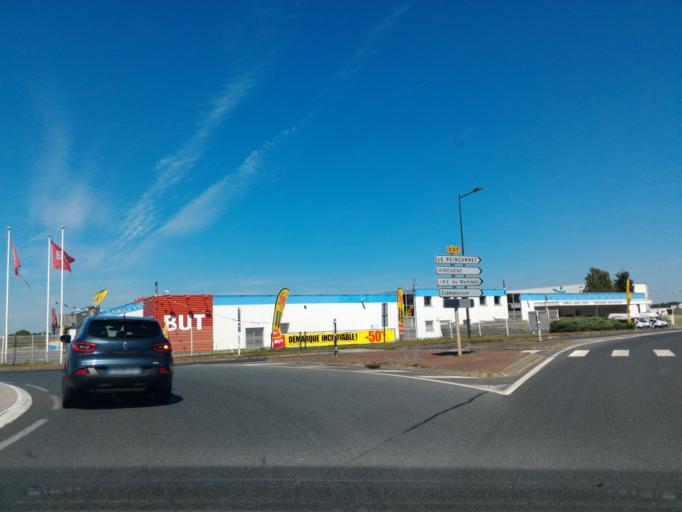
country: FR
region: Centre
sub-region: Departement de l'Indre
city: Saint-Maur
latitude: 46.7752
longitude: 1.6486
